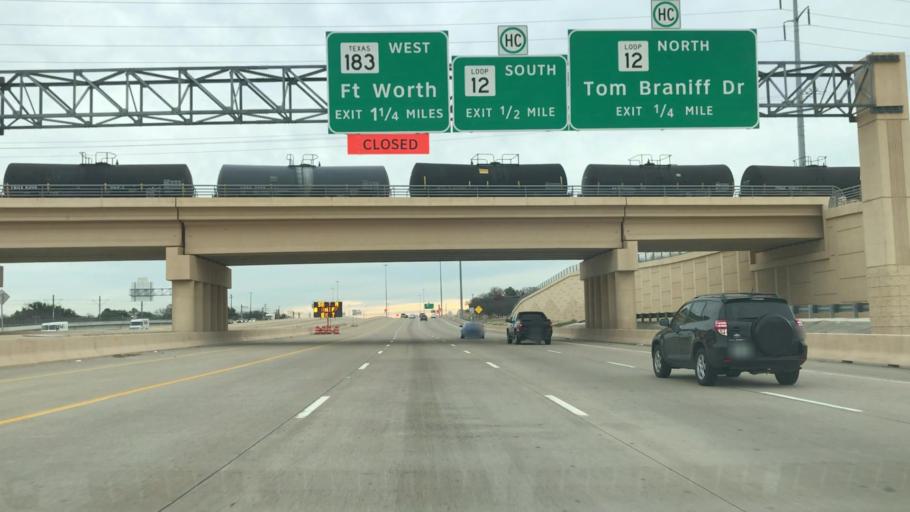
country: US
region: Texas
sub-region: Dallas County
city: Irving
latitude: 32.8545
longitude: -96.9271
